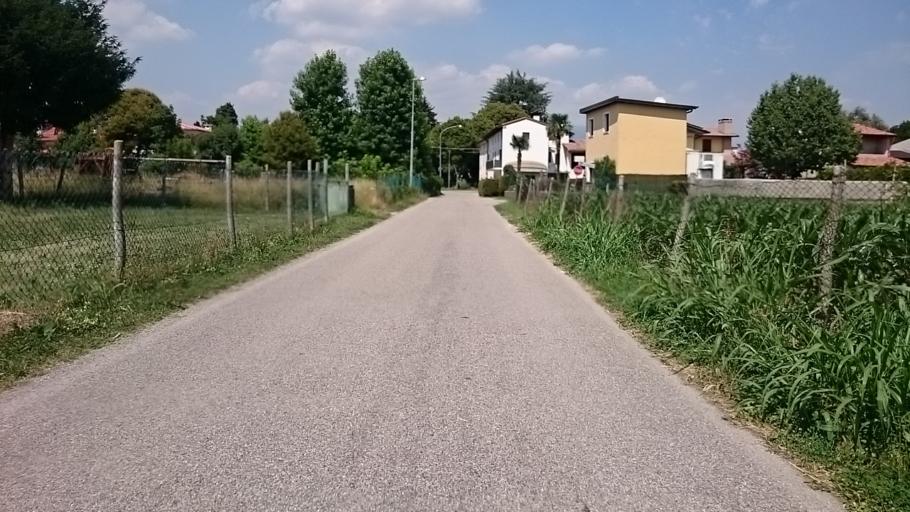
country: IT
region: Veneto
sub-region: Provincia di Vicenza
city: Rosa
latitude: 45.7258
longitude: 11.7348
